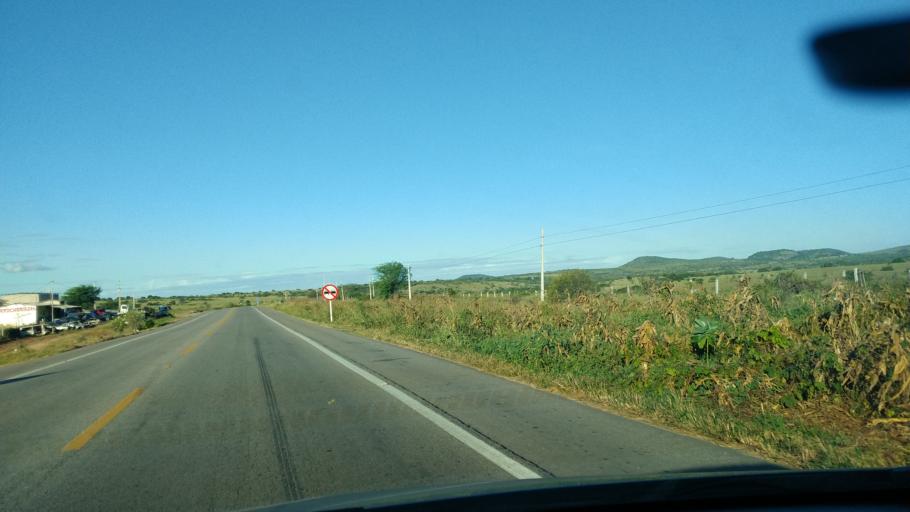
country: BR
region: Rio Grande do Norte
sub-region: Tangara
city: Tangara
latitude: -6.1893
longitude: -35.7845
